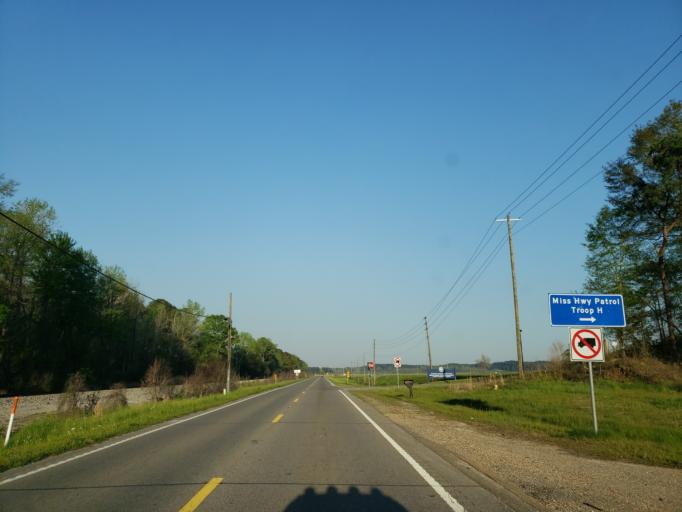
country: US
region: Mississippi
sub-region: Lauderdale County
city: Marion
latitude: 32.3941
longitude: -88.6375
